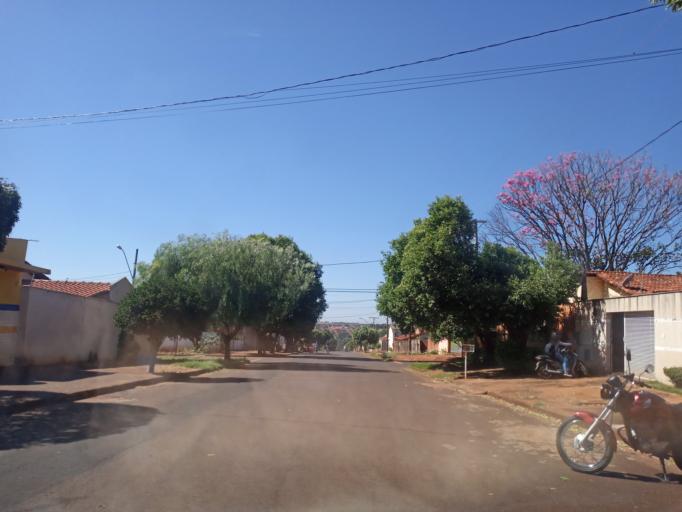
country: BR
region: Minas Gerais
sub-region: Ituiutaba
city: Ituiutaba
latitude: -18.9900
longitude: -49.4498
